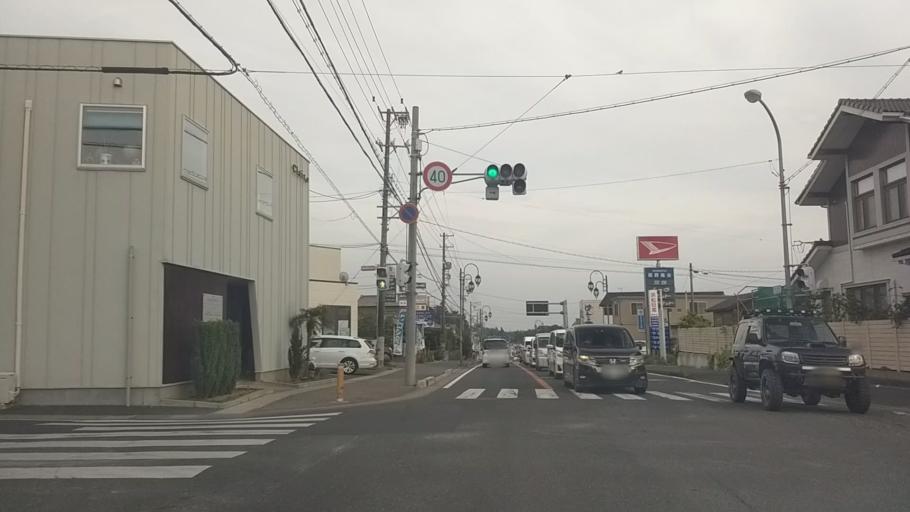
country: JP
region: Shizuoka
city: Hamamatsu
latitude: 34.7329
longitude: 137.6885
